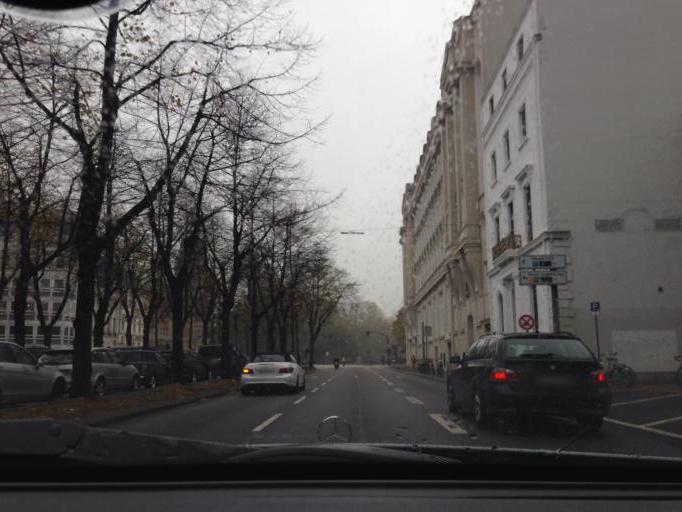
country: DE
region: Hamburg
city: Neustadt
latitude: 53.5580
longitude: 9.9913
